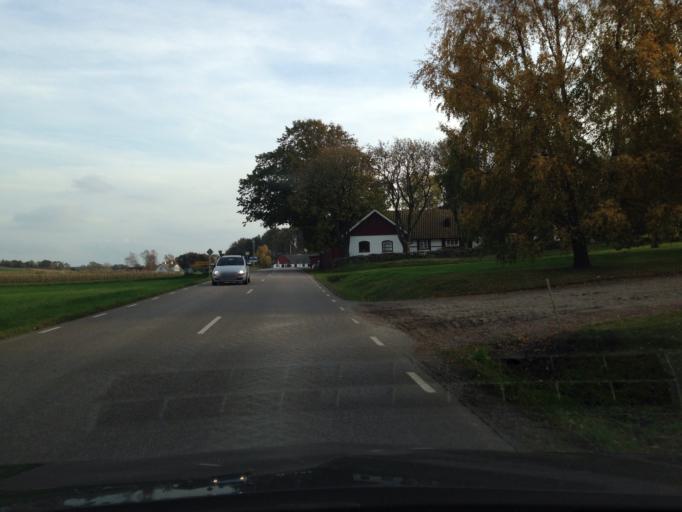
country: SE
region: Skane
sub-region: Angelholms Kommun
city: Vejbystrand
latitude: 56.4257
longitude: 12.7319
